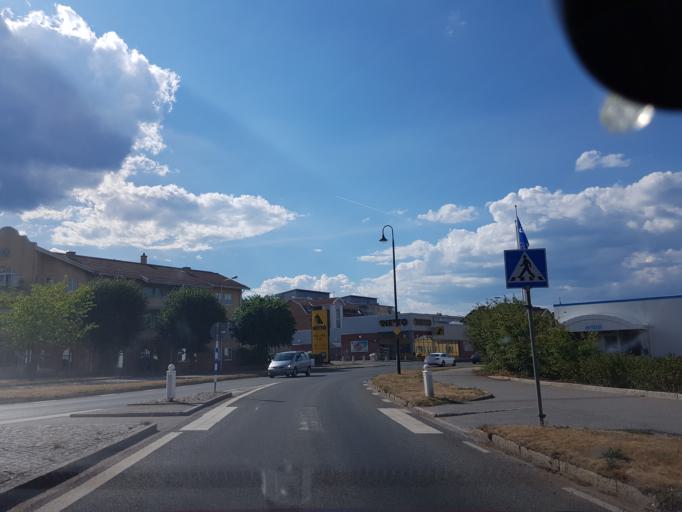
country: SE
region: Joenkoeping
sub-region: Gislaveds Kommun
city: Gislaved
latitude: 57.3017
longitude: 13.5450
